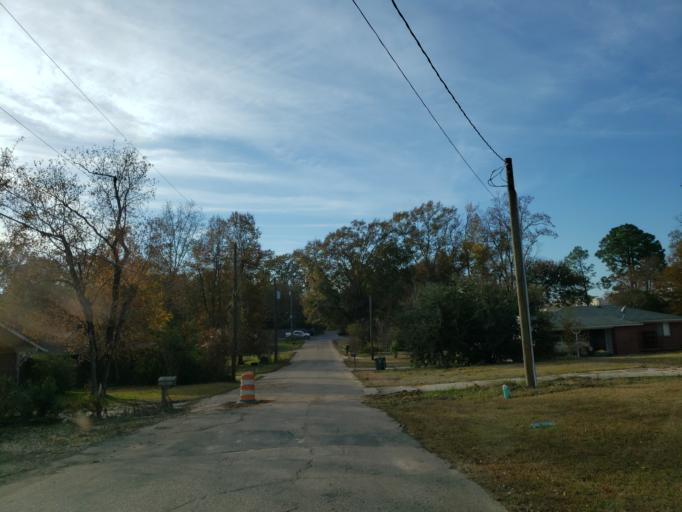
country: US
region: Mississippi
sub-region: Lamar County
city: West Hattiesburg
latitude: 31.3221
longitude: -89.3424
